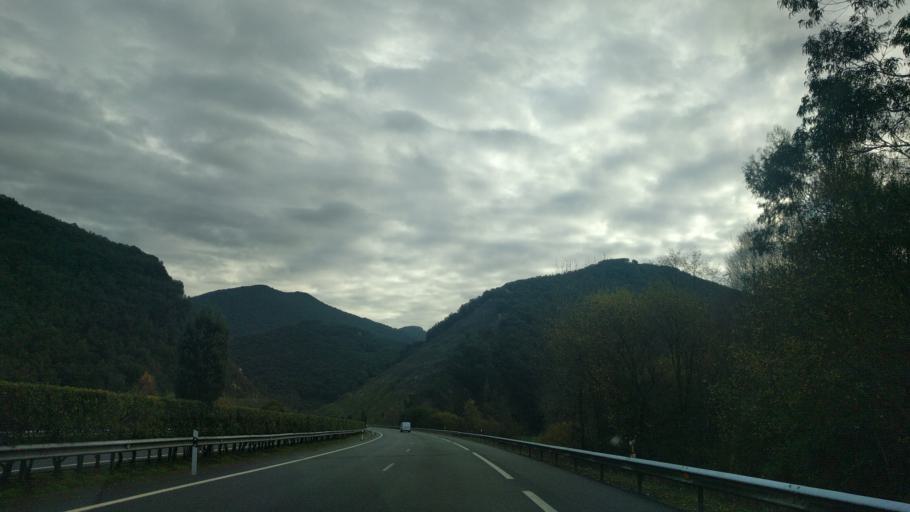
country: ES
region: Cantabria
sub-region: Provincia de Cantabria
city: Liendo
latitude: 43.3816
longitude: -3.3797
